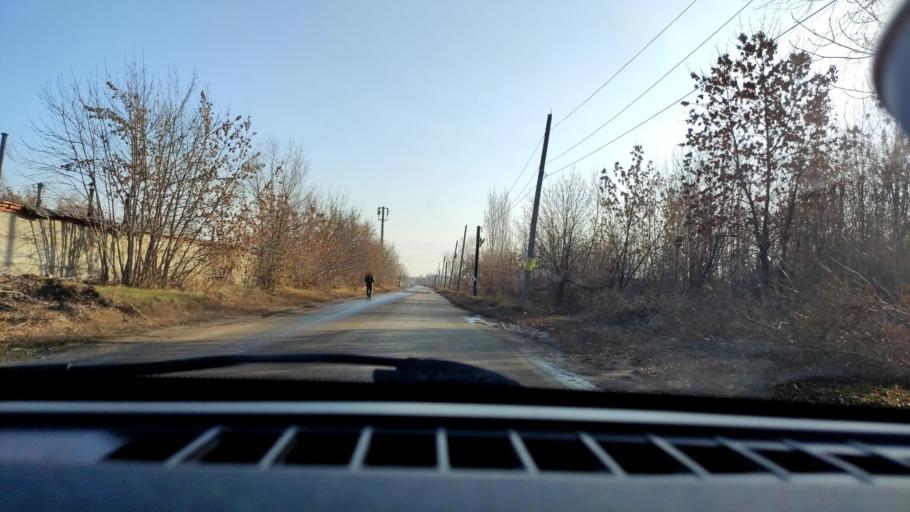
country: RU
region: Samara
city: Samara
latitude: 53.1196
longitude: 50.0984
